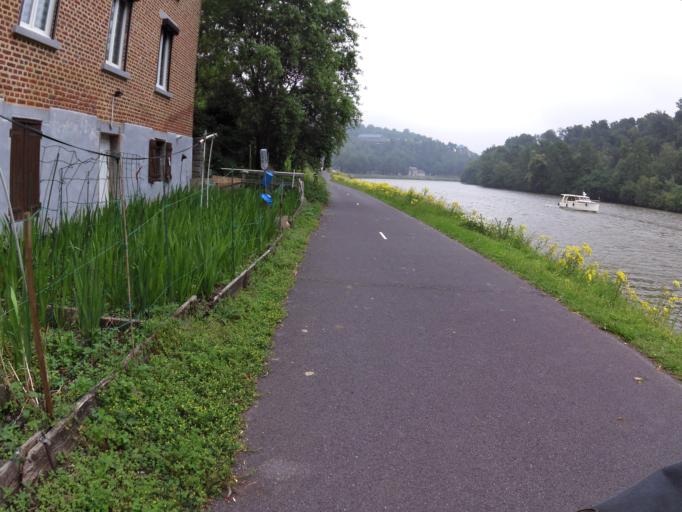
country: FR
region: Champagne-Ardenne
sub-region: Departement des Ardennes
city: Fumay
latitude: 49.9852
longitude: 4.6936
